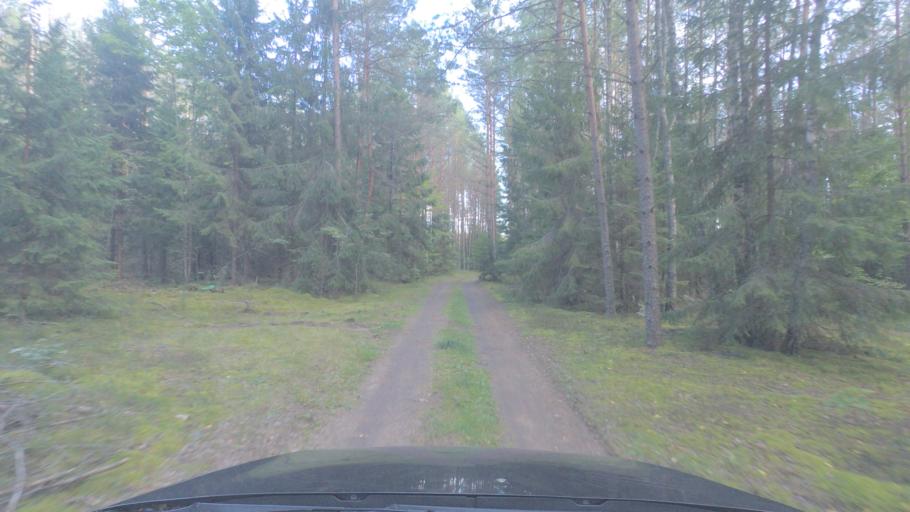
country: LT
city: Svencioneliai
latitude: 55.1606
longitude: 25.8522
